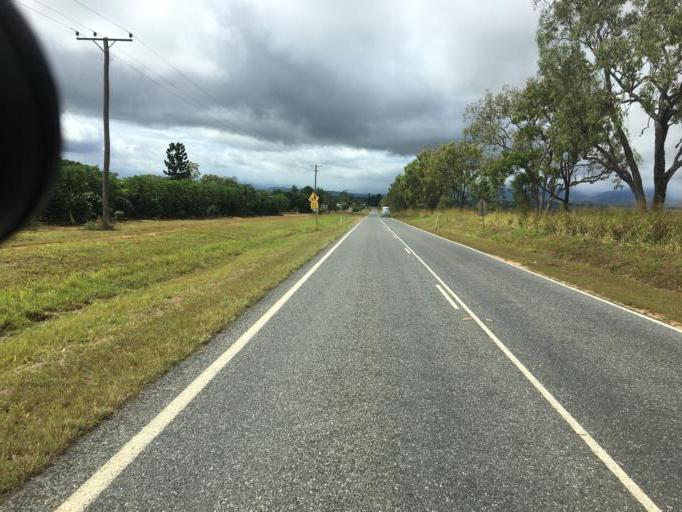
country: AU
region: Queensland
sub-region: Tablelands
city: Mareeba
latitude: -17.0162
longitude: 145.3541
